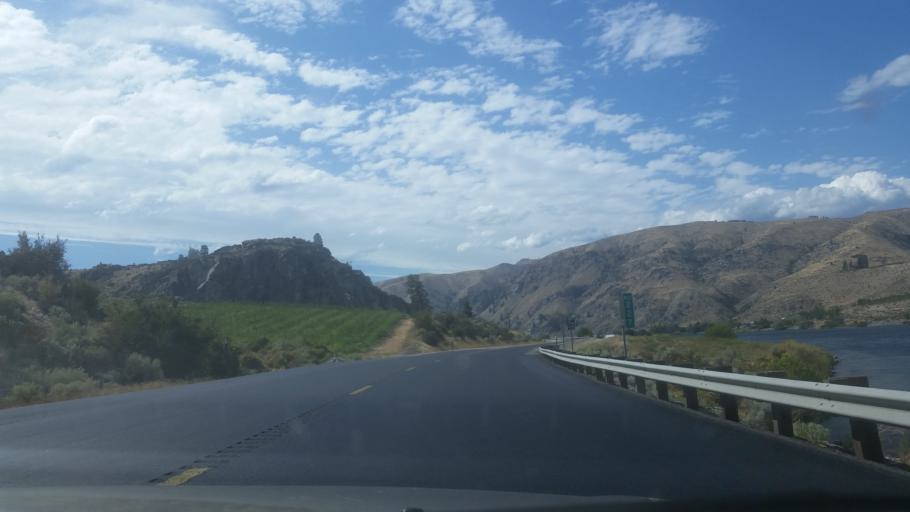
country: US
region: Washington
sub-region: Chelan County
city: Chelan
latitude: 47.7632
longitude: -120.0987
